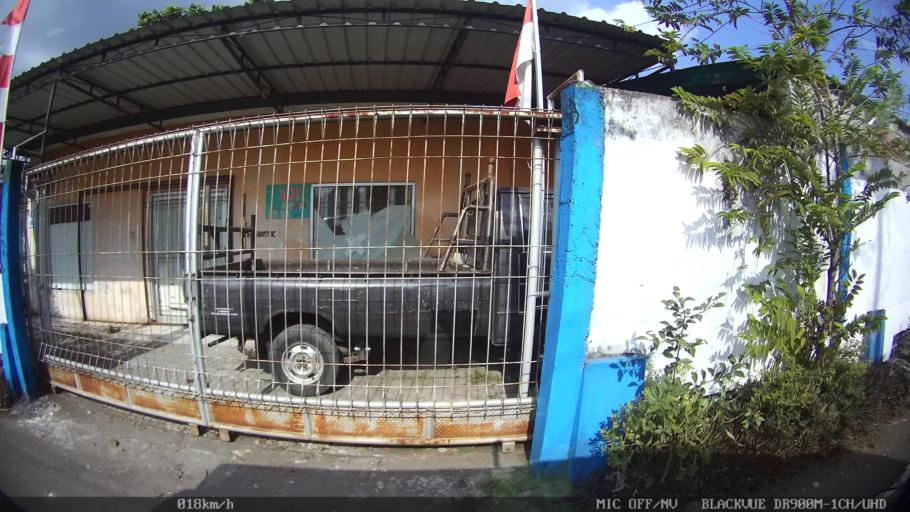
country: ID
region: Daerah Istimewa Yogyakarta
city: Gamping Lor
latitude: -7.7976
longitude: 110.3419
